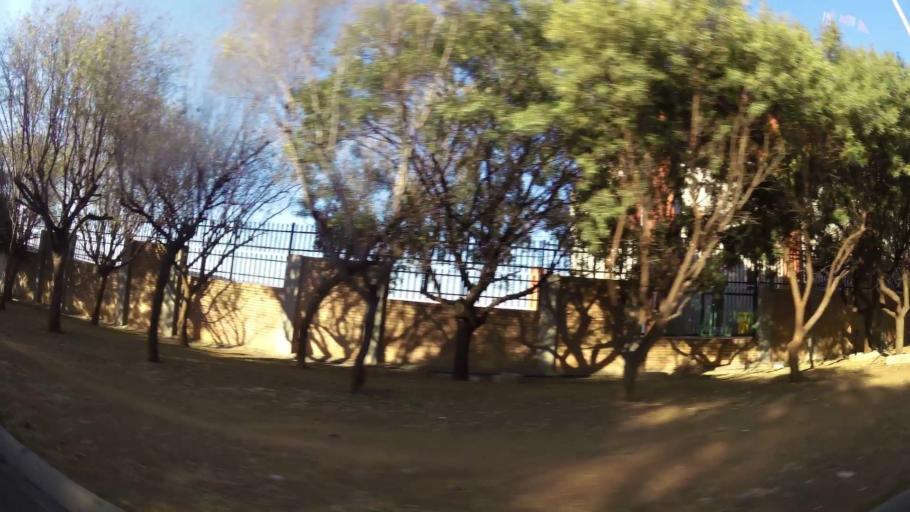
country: ZA
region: Gauteng
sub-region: City of Tshwane Metropolitan Municipality
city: Centurion
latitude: -25.8732
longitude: 28.1357
